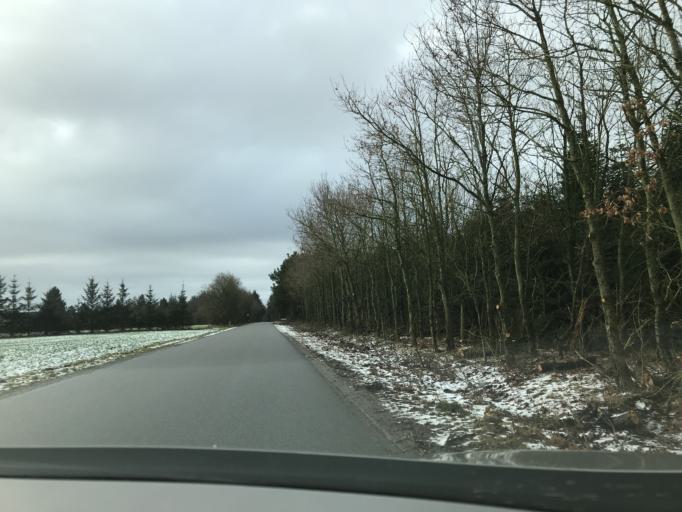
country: DK
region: South Denmark
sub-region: Varde Kommune
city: Oksbol
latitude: 55.7555
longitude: 8.2756
